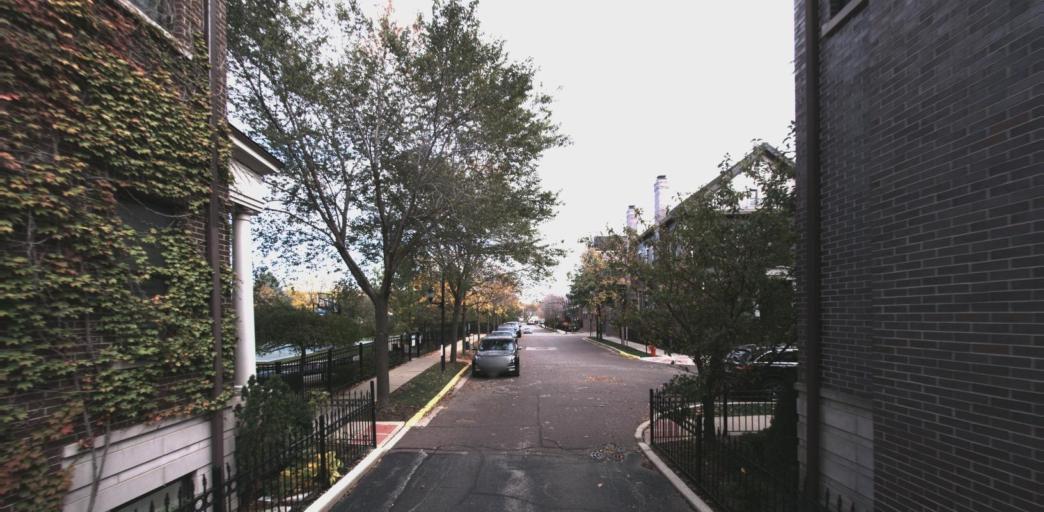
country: US
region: Illinois
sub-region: Cook County
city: Chicago
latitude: 41.9311
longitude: -87.6730
